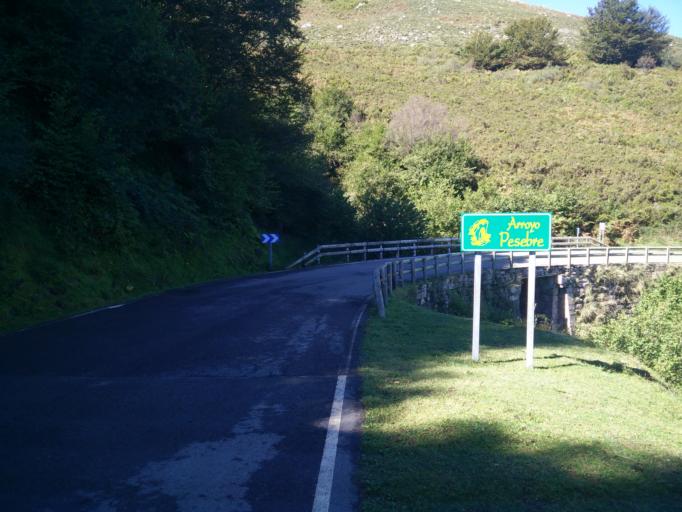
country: ES
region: Cantabria
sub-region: Provincia de Cantabria
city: Reinosa
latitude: 43.0684
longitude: -4.2341
